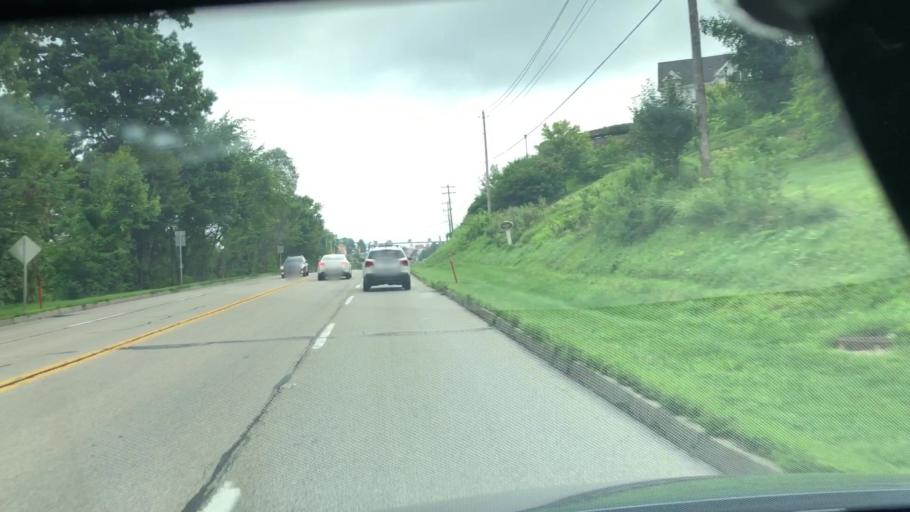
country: US
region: Pennsylvania
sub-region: Allegheny County
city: Mount Lebanon
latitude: 40.3420
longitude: -80.0620
